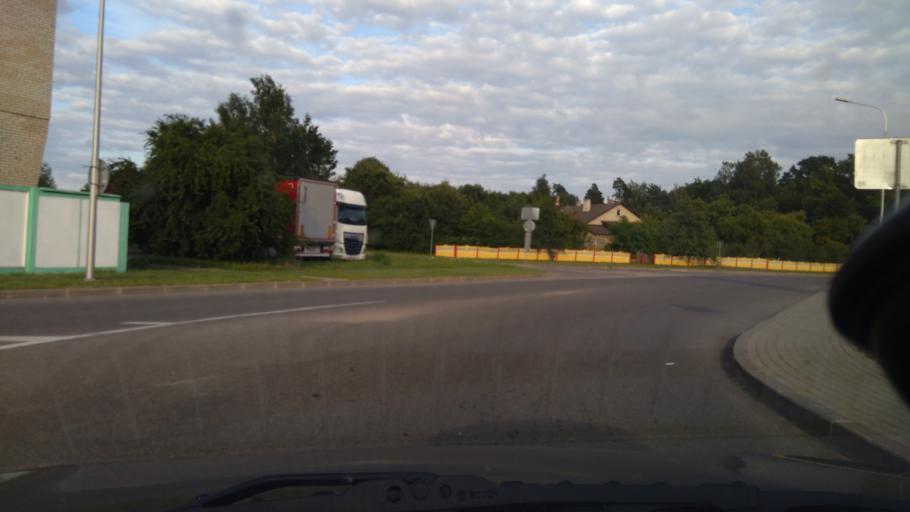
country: BY
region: Grodnenskaya
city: Masty
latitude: 53.4184
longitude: 24.5662
